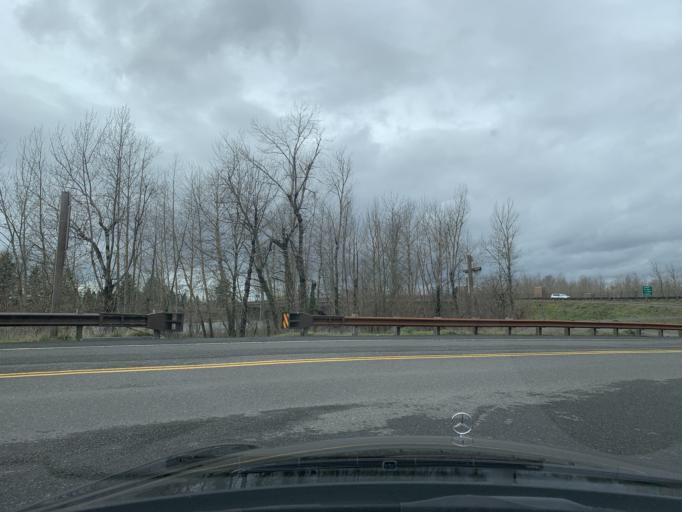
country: US
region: Oregon
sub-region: Multnomah County
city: Troutdale
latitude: 45.5434
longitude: -122.3815
